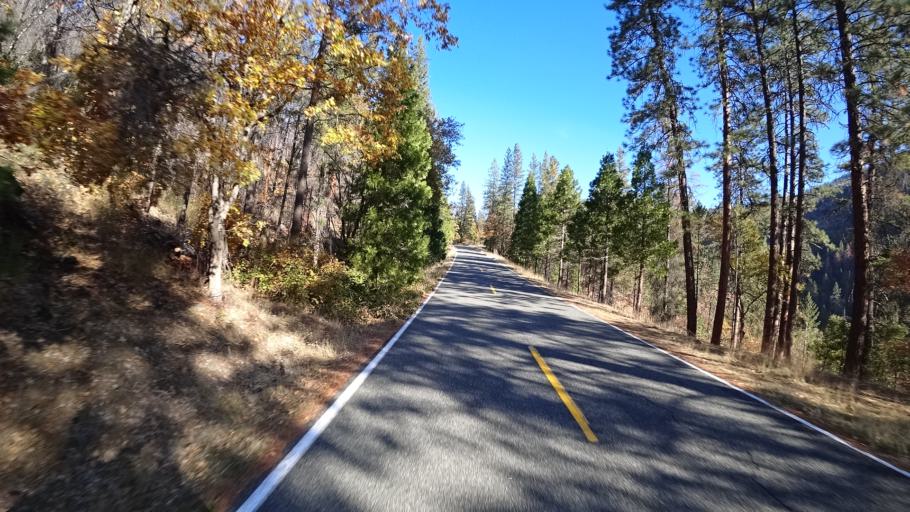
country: US
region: California
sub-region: Siskiyou County
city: Yreka
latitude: 41.8862
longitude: -122.8234
